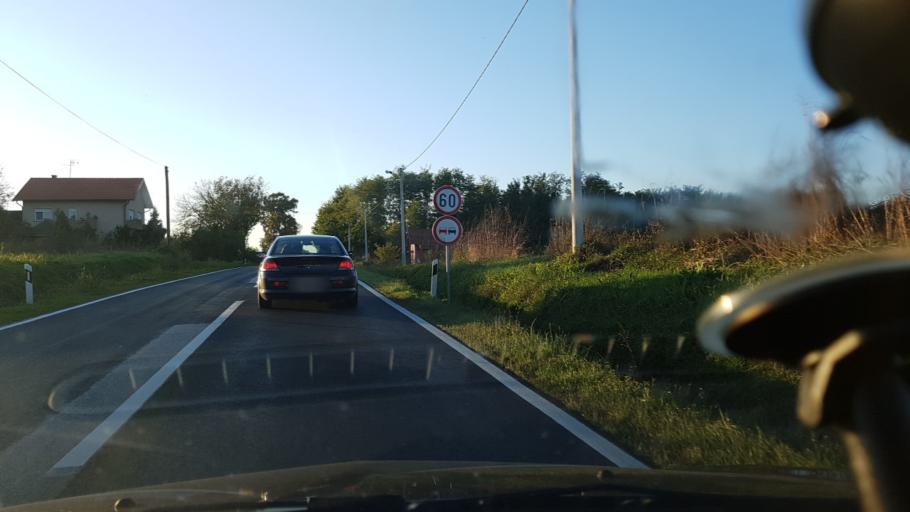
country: HR
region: Koprivnicko-Krizevacka
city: Hlebine
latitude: 46.1095
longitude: 16.8994
